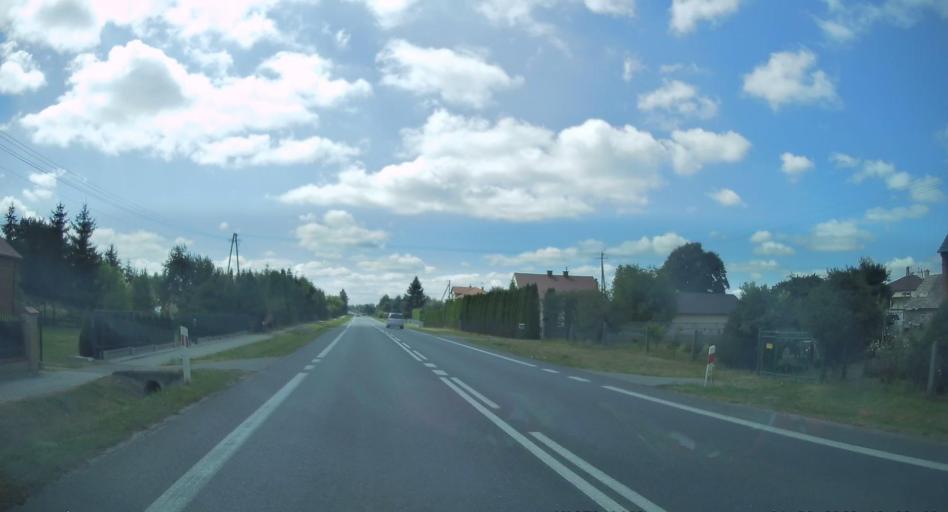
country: PL
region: Subcarpathian Voivodeship
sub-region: Powiat mielecki
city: Przeclaw
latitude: 50.1795
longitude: 21.4957
